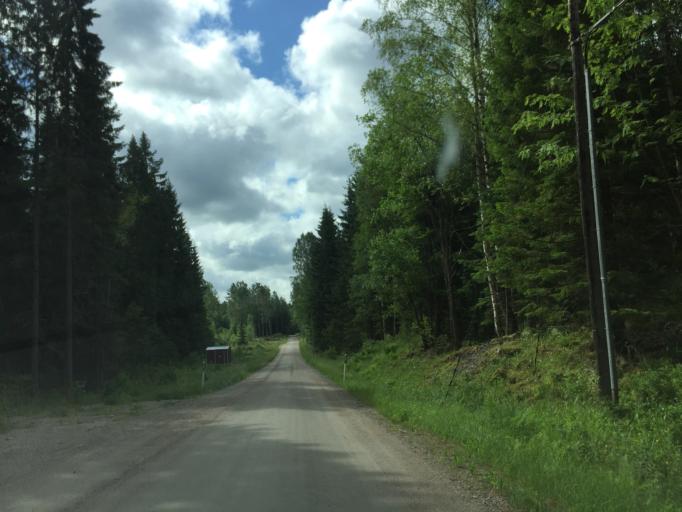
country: SE
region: OErebro
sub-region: Lekebergs Kommun
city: Fjugesta
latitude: 59.2727
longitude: 14.7953
